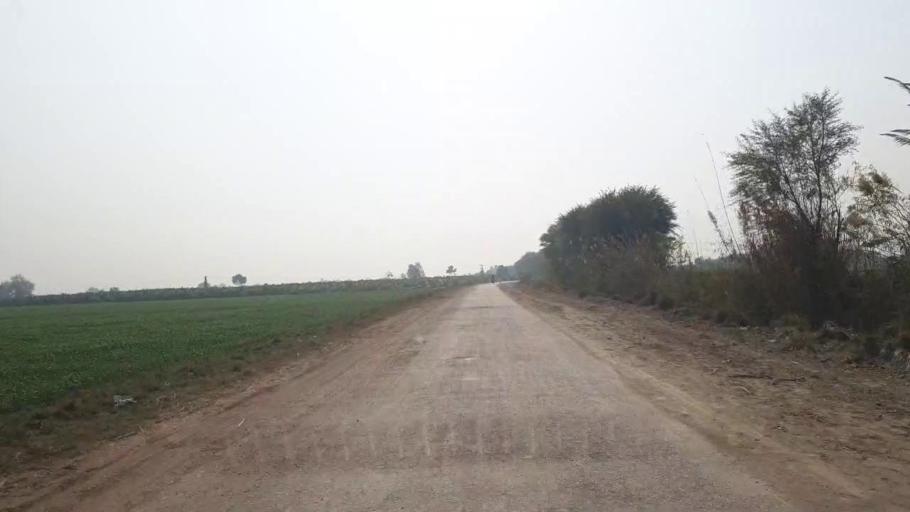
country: PK
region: Sindh
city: Hala
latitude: 25.9057
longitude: 68.4460
